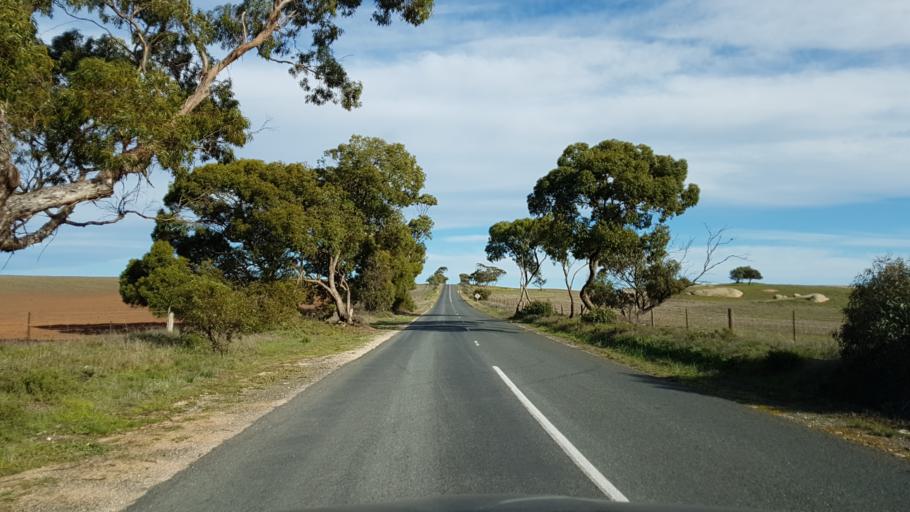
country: AU
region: South Australia
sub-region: Murray Bridge
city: Tailem Bend
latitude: -35.1832
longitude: 139.4648
